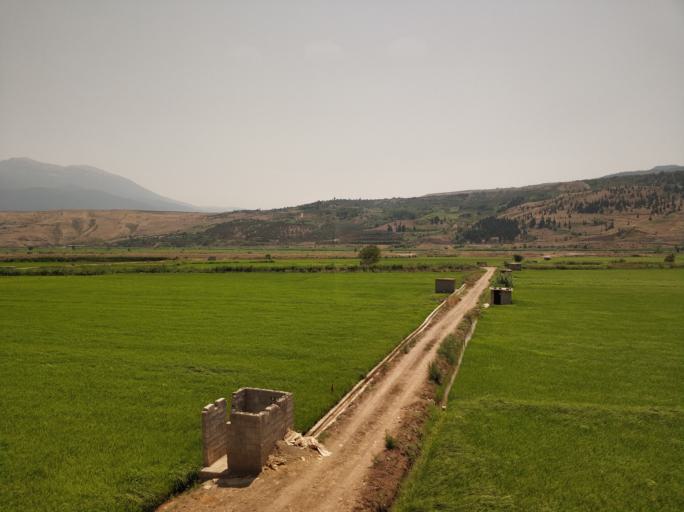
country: IR
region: Gilan
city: Pa'in-e Bazar-e Rudbar
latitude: 36.8743
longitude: 49.4937
